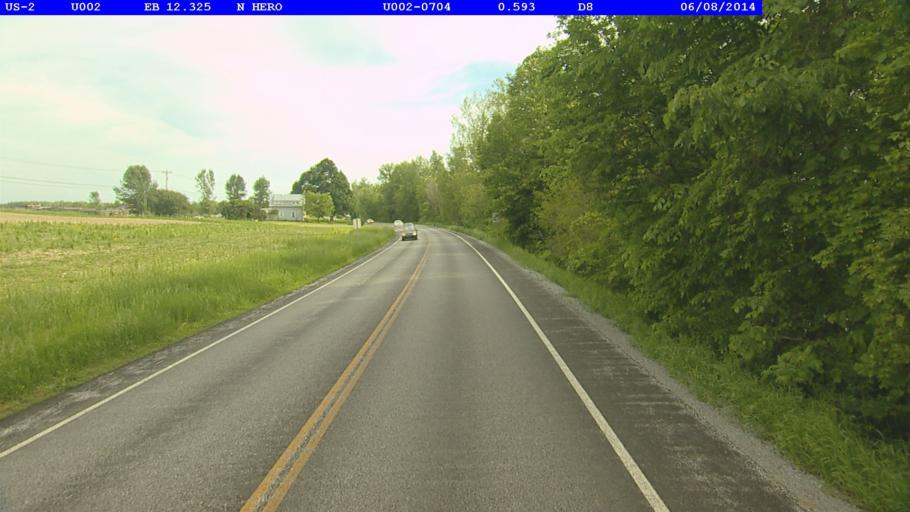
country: US
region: Vermont
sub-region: Grand Isle County
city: North Hero
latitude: 44.8778
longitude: -73.2720
